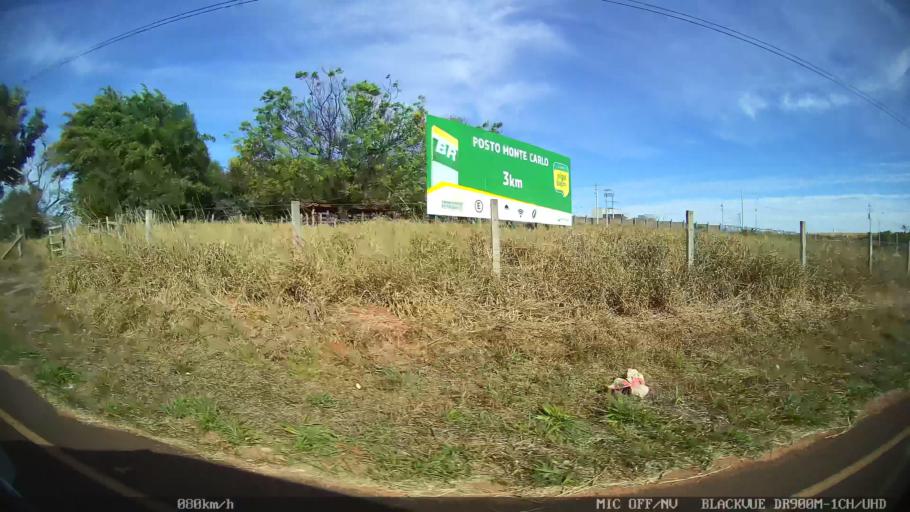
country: BR
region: Sao Paulo
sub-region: Sao Jose Do Rio Preto
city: Sao Jose do Rio Preto
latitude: -20.7973
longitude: -49.3219
